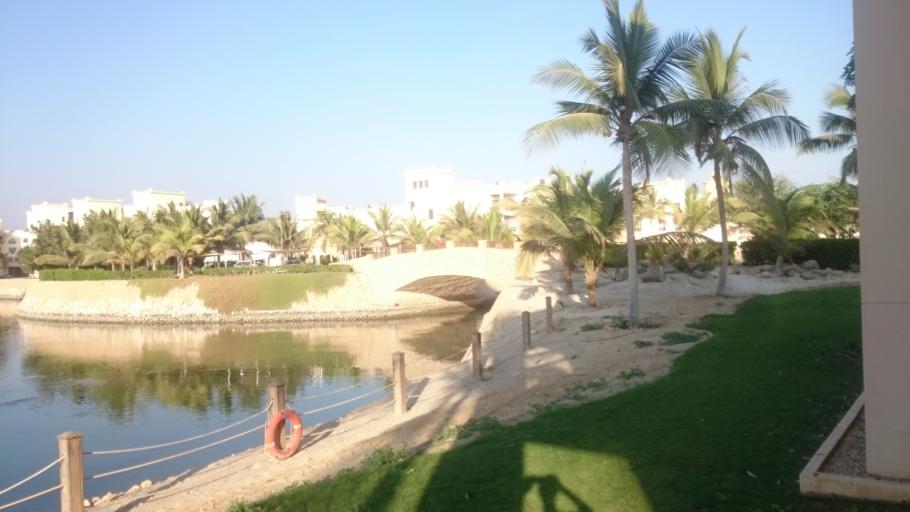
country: OM
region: Zufar
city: Salalah
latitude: 17.0315
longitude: 54.2998
